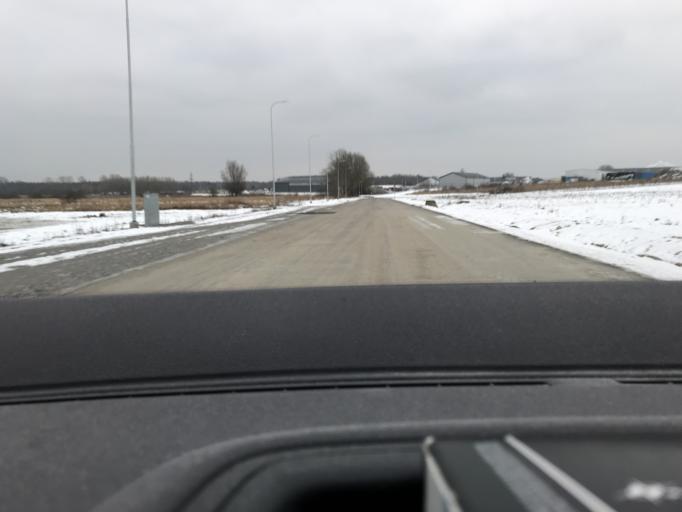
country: SE
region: Skane
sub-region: Ystads Kommun
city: Ystad
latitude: 55.4487
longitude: 13.8552
